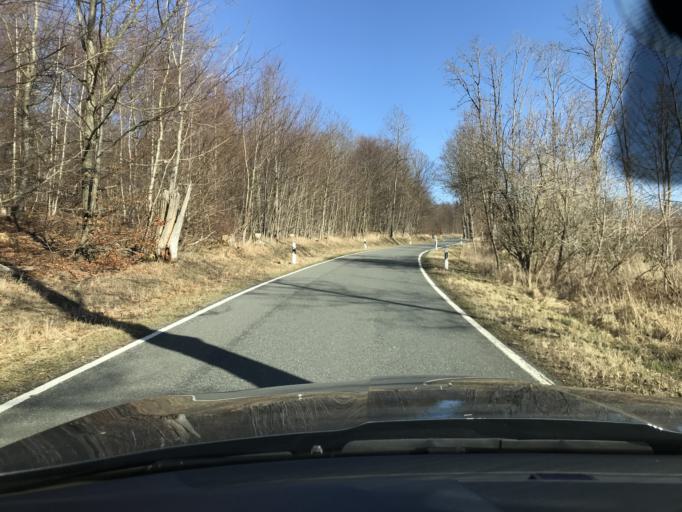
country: DE
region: Saxony-Anhalt
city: Timmenrode
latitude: 51.7324
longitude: 10.9795
